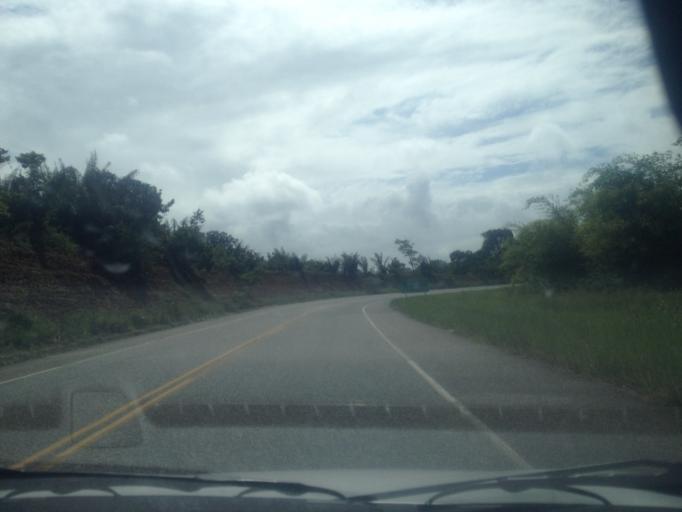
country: BR
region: Bahia
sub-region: Conde
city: Conde
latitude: -11.7613
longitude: -37.5905
